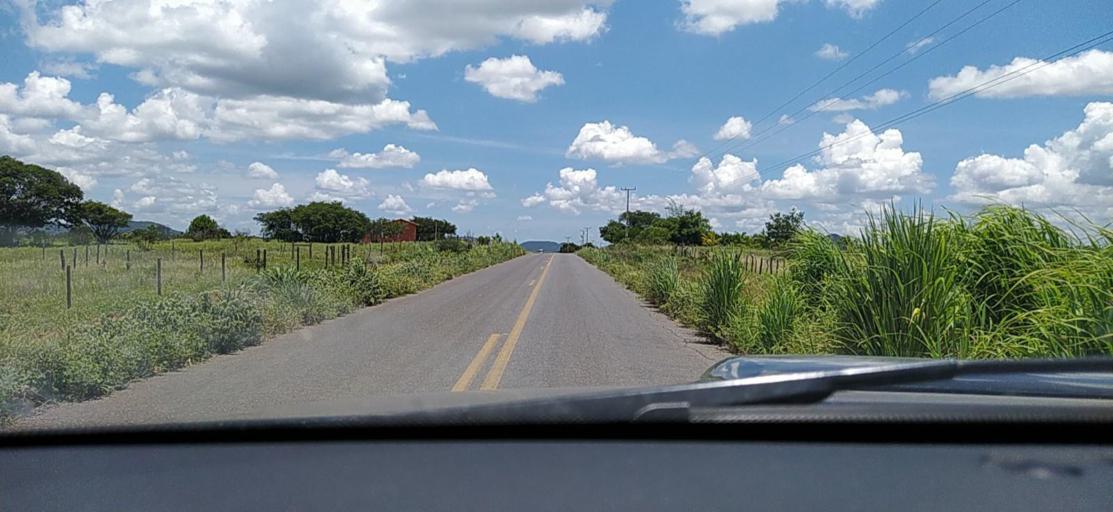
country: BR
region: Bahia
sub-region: Guanambi
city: Guanambi
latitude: -14.1063
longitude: -42.8673
